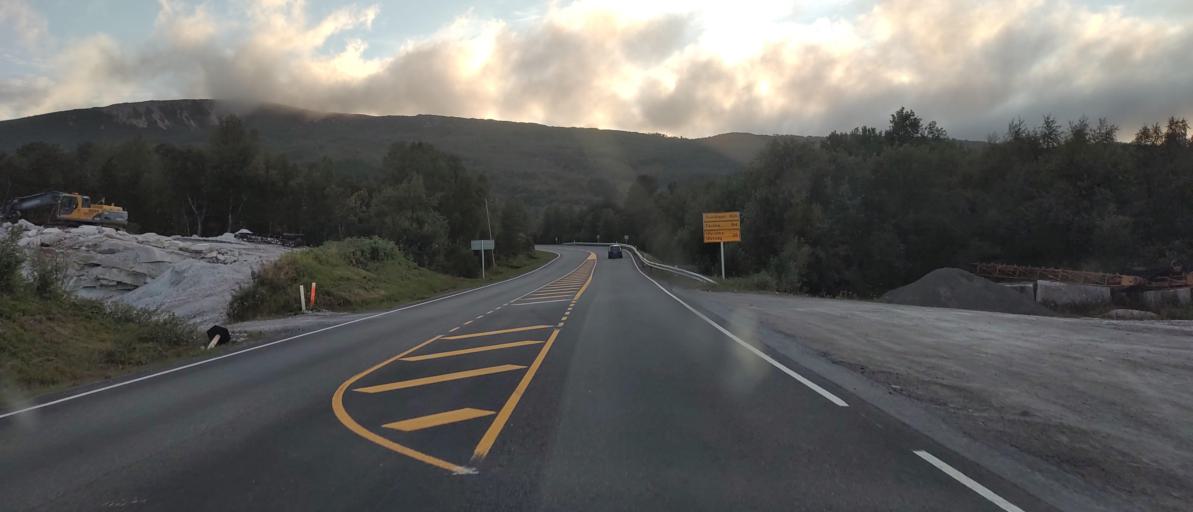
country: NO
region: Nordland
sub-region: Lodingen
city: Lodingen
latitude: 68.2176
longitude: 16.0575
